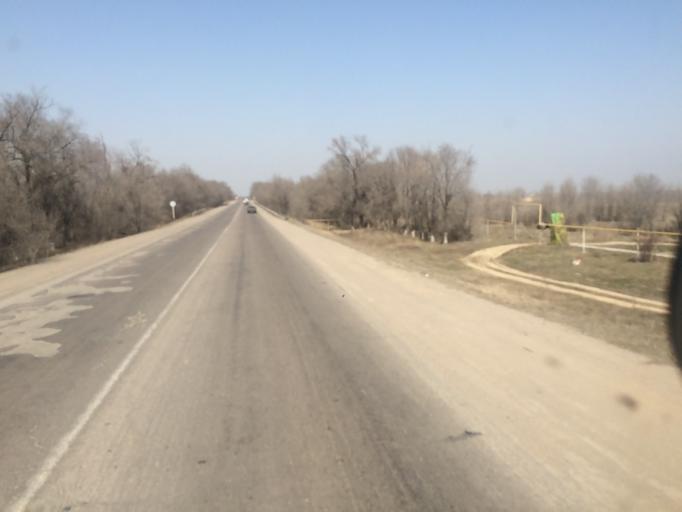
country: KZ
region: Almaty Oblysy
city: Burunday
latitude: 43.3115
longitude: 76.6658
